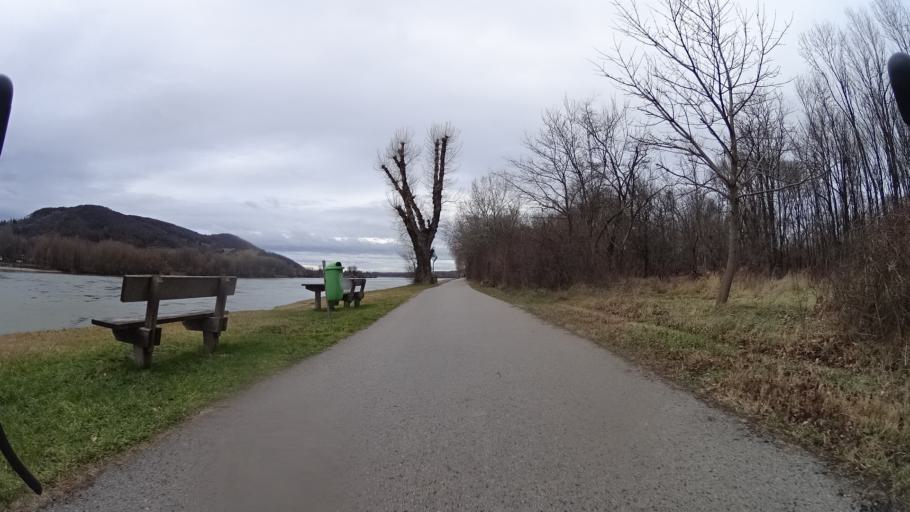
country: AT
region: Lower Austria
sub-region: Politischer Bezirk Korneuburg
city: Korneuburg
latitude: 48.3456
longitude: 16.3038
